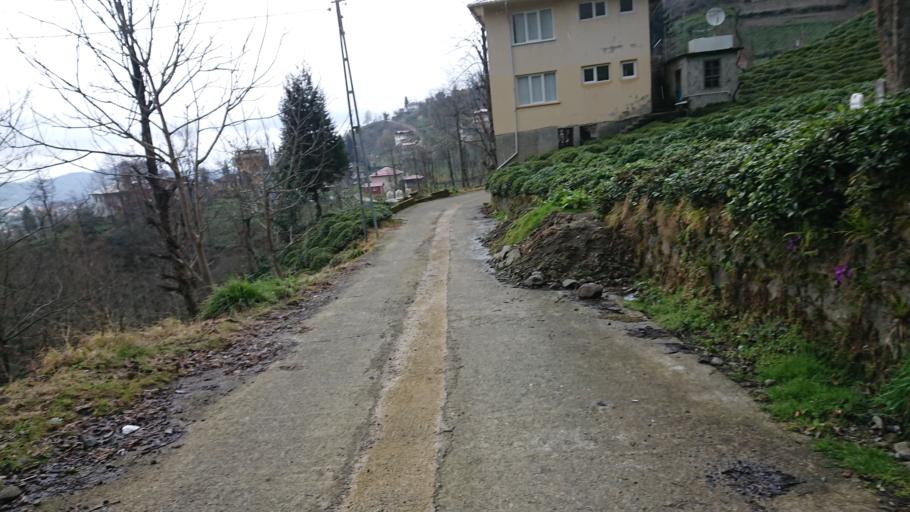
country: TR
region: Rize
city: Rize
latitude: 40.9796
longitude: 40.4961
